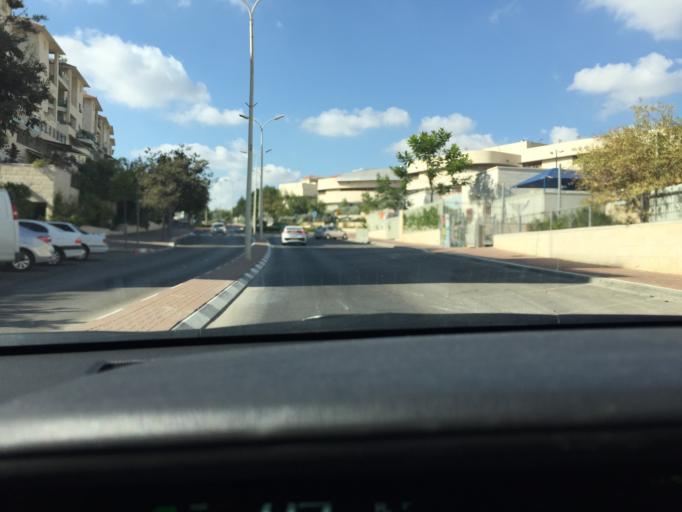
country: PS
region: West Bank
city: Budrus
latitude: 32.0034
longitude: 34.9492
